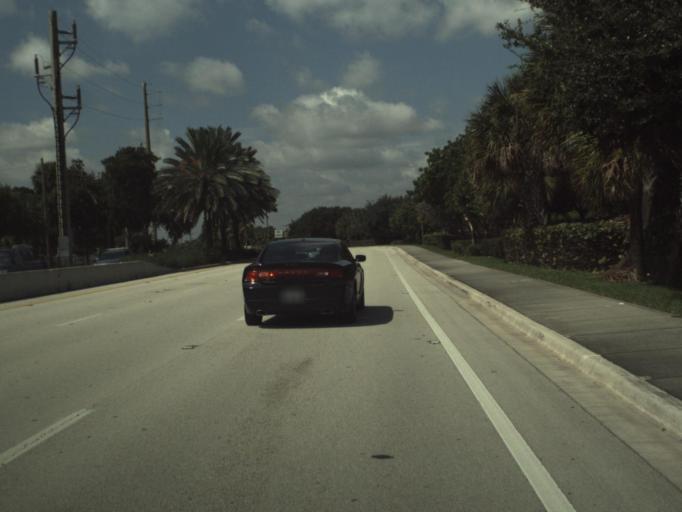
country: US
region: Florida
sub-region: Palm Beach County
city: Jupiter
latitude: 26.9453
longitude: -80.0920
